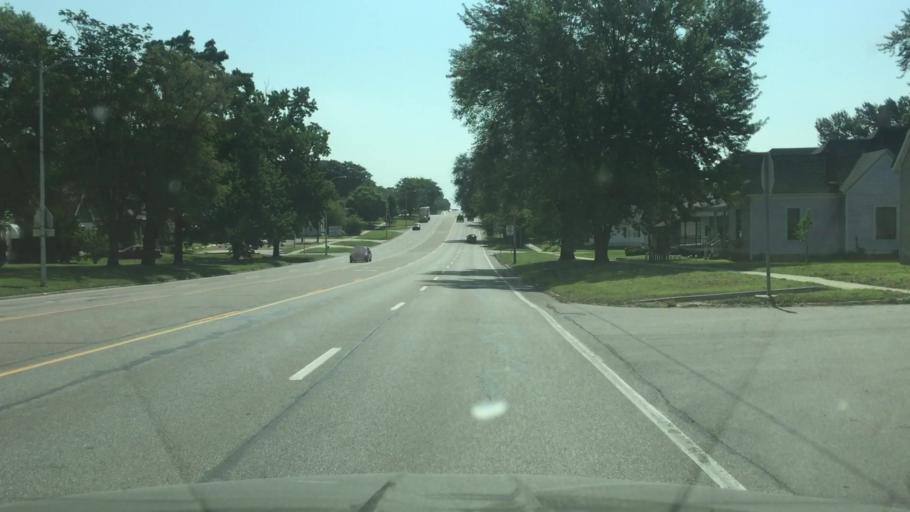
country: US
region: Missouri
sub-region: Pettis County
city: Sedalia
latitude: 38.7035
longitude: -93.2124
